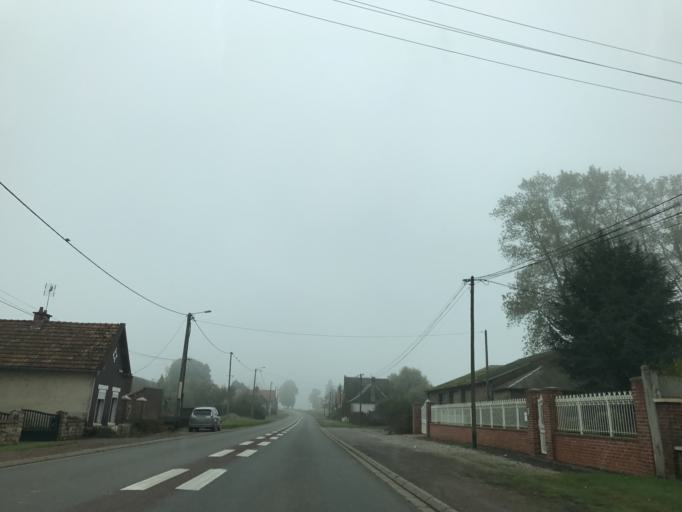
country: FR
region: Nord-Pas-de-Calais
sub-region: Departement du Pas-de-Calais
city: Bapaume
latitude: 50.0583
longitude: 2.8972
